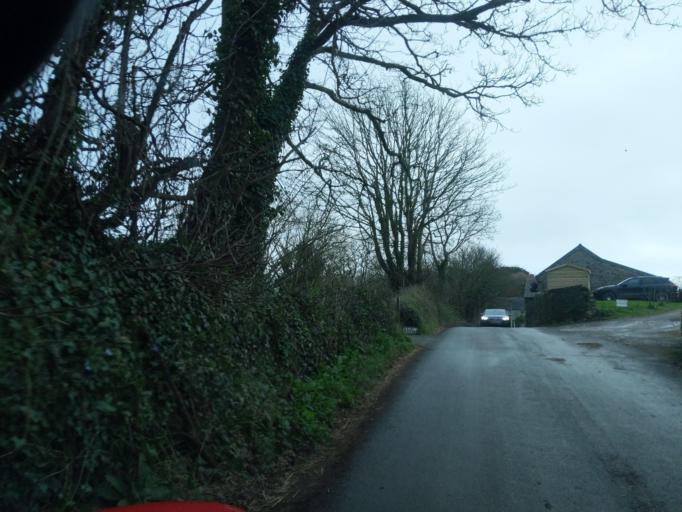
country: GB
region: England
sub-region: Devon
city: Wembury
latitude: 50.3274
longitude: -4.0881
